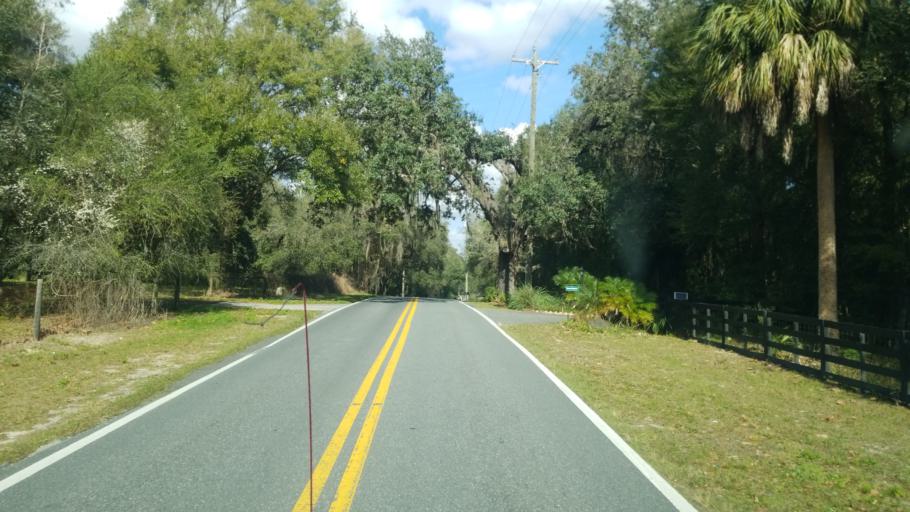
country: US
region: Florida
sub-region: Citrus County
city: Floral City
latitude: 28.7420
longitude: -82.2639
